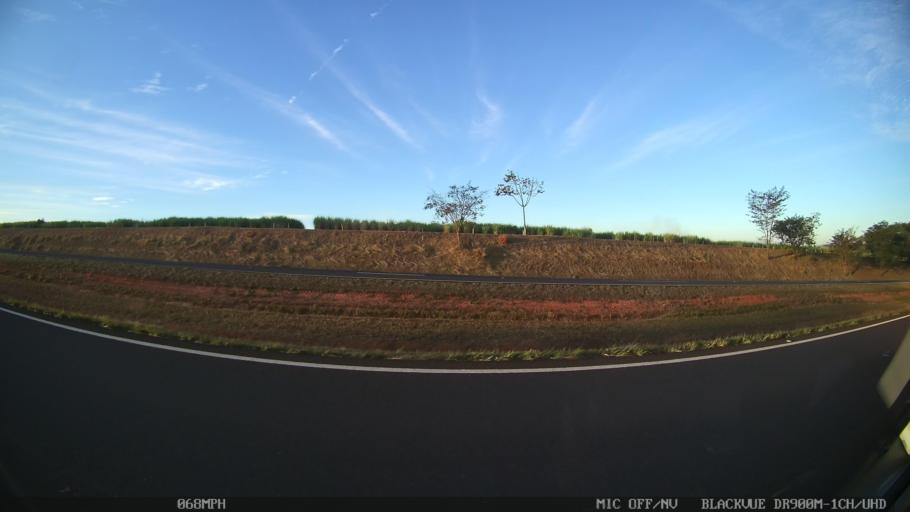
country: BR
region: Sao Paulo
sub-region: Catanduva
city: Catanduva
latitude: -21.1121
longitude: -49.0485
